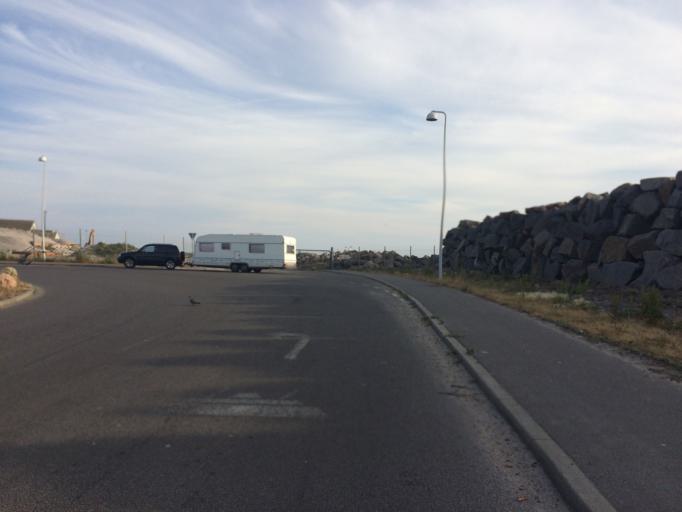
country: DK
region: Capital Region
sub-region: Bornholm Kommune
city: Ronne
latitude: 55.1015
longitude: 14.6849
